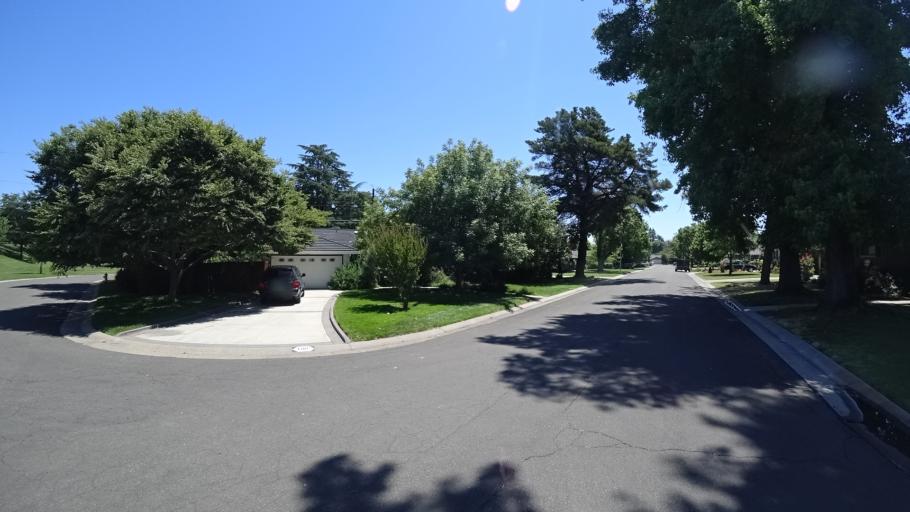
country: US
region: California
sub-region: Yolo County
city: West Sacramento
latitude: 38.5387
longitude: -121.5115
